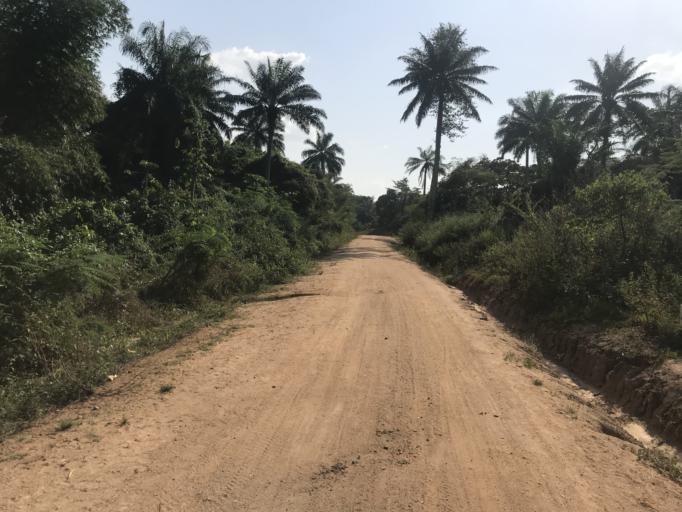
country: NG
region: Osun
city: Ikirun
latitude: 7.8786
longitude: 4.5858
